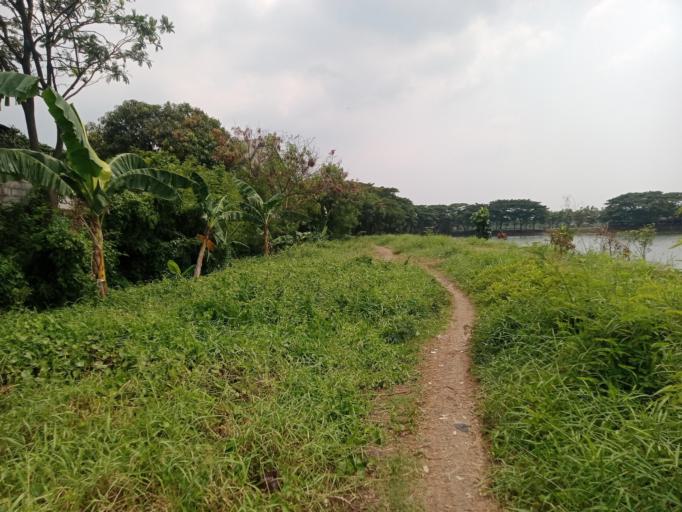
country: ID
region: Banten
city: Tangerang
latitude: -6.1644
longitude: 106.5898
